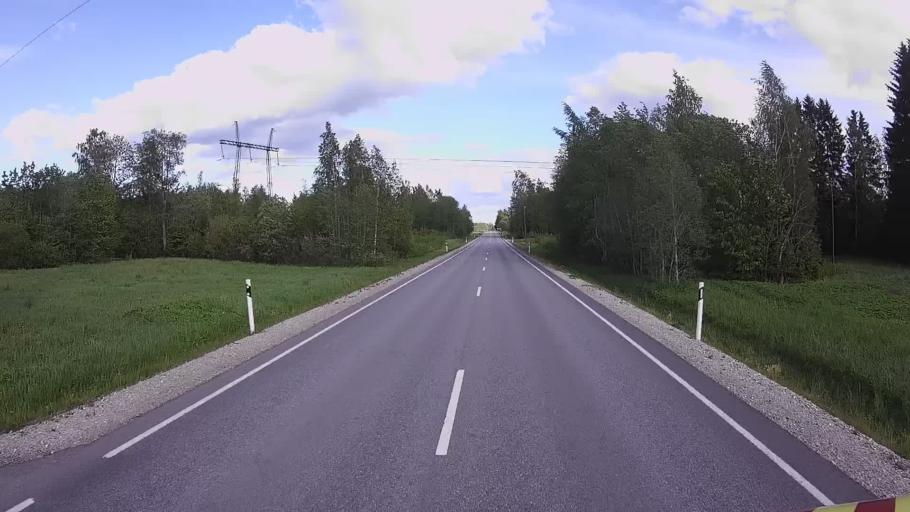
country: EE
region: Jogevamaa
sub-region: Mustvee linn
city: Mustvee
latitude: 58.8686
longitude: 26.8313
